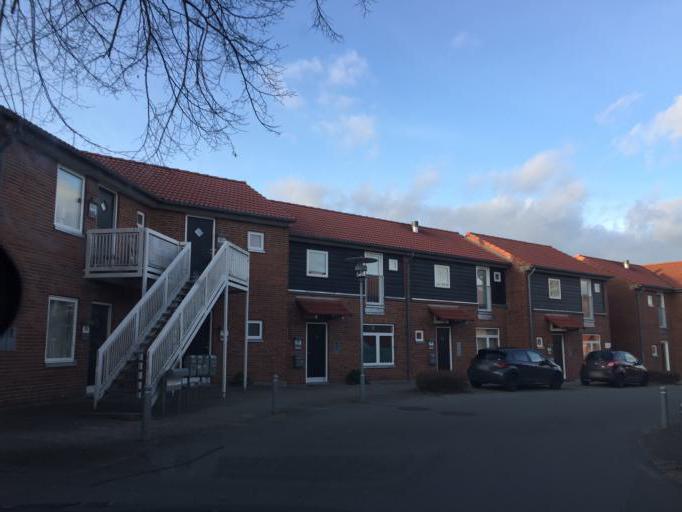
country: DK
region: South Denmark
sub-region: Odense Kommune
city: Neder Holluf
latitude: 55.3764
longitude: 10.4599
